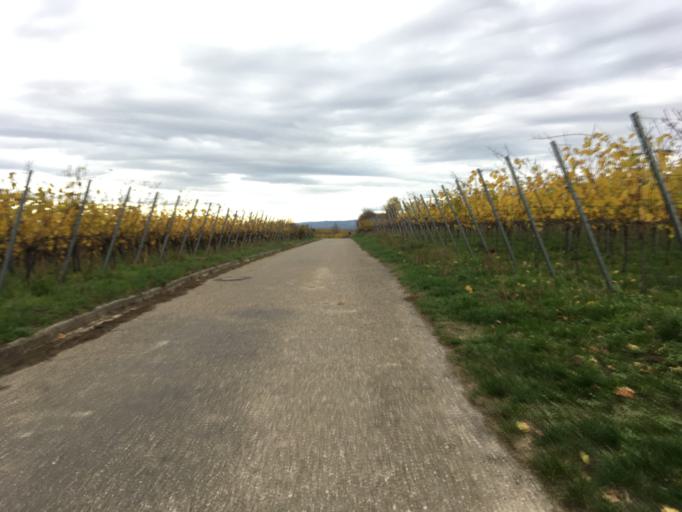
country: DE
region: Baden-Wuerttemberg
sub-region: Freiburg Region
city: Merdingen
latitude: 48.0255
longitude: 7.7052
